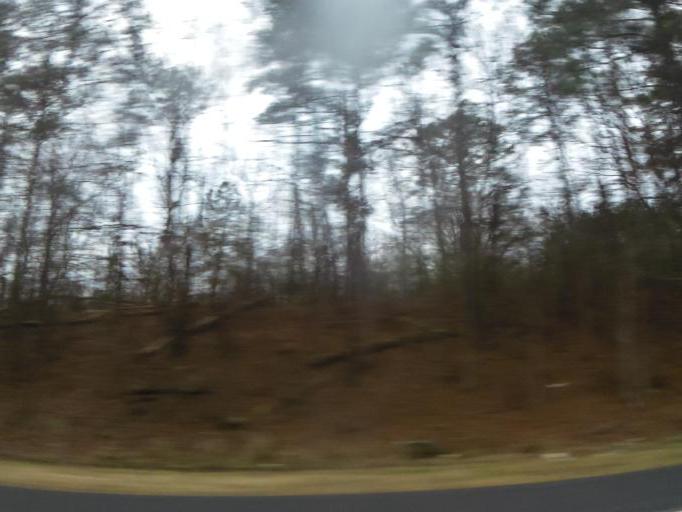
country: US
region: Alabama
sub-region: Blount County
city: Smoke Rise
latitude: 33.8679
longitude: -86.8344
